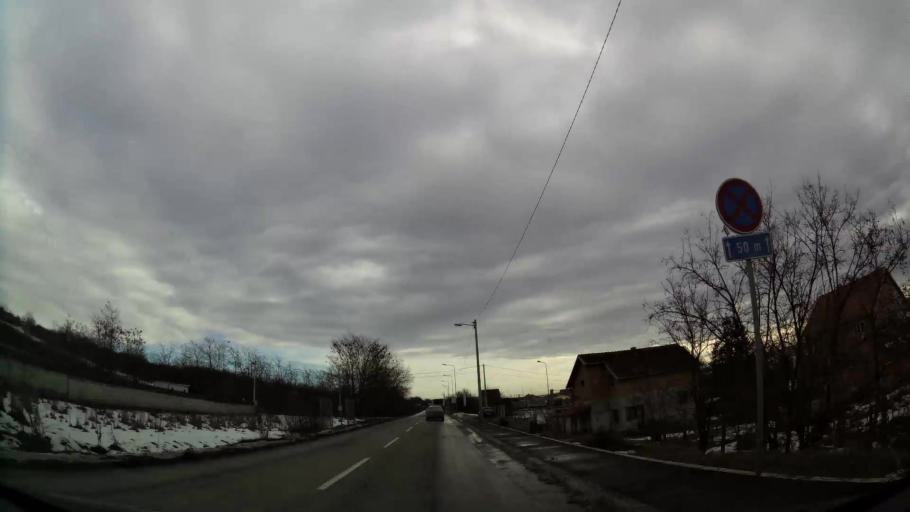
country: RS
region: Central Serbia
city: Sremcica
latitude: 44.7236
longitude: 20.3972
